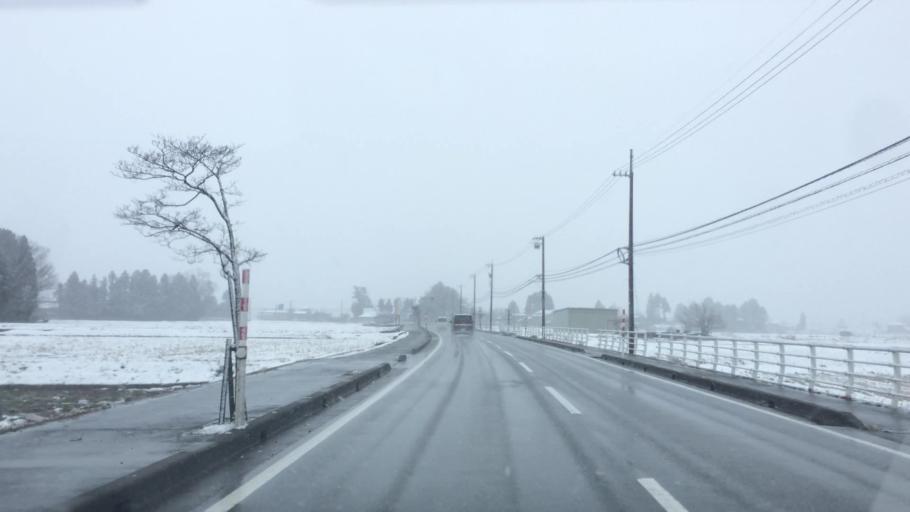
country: JP
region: Toyama
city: Toyama-shi
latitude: 36.6299
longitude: 137.2248
